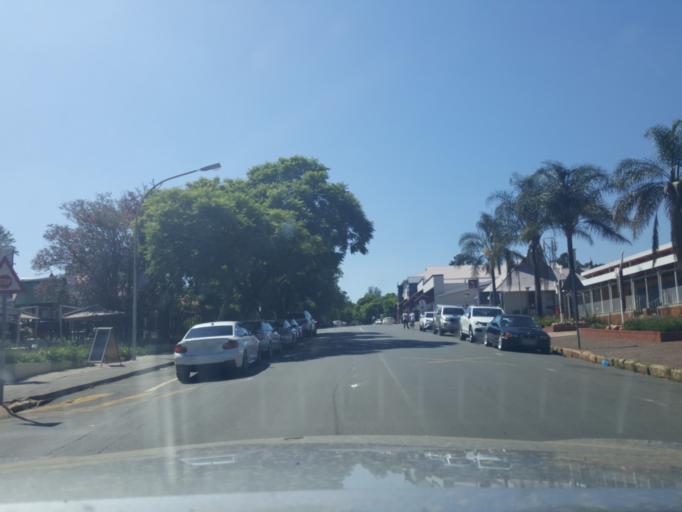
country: ZA
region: Gauteng
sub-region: City of Tshwane Metropolitan Municipality
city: Cullinan
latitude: -25.6718
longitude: 28.5192
